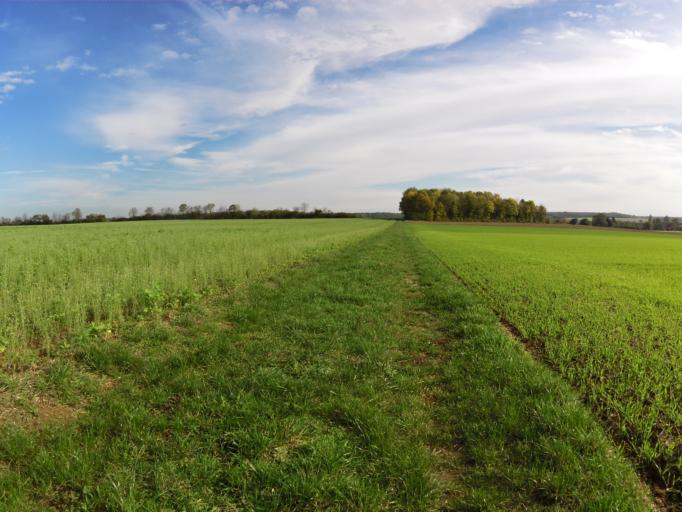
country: DE
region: Bavaria
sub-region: Regierungsbezirk Unterfranken
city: Sommerhausen
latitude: 49.7117
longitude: 10.0696
